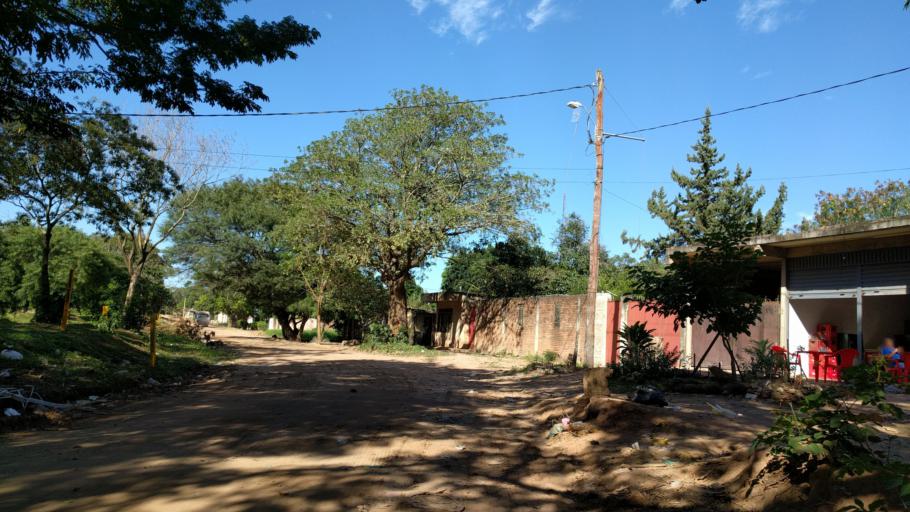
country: BO
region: Santa Cruz
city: Santa Cruz de la Sierra
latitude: -17.7893
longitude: -63.2247
